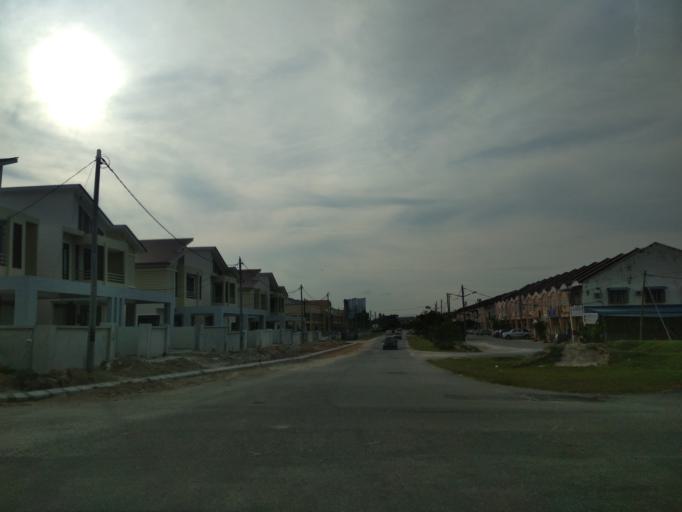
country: MY
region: Perak
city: Kampar
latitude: 4.3159
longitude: 101.1427
